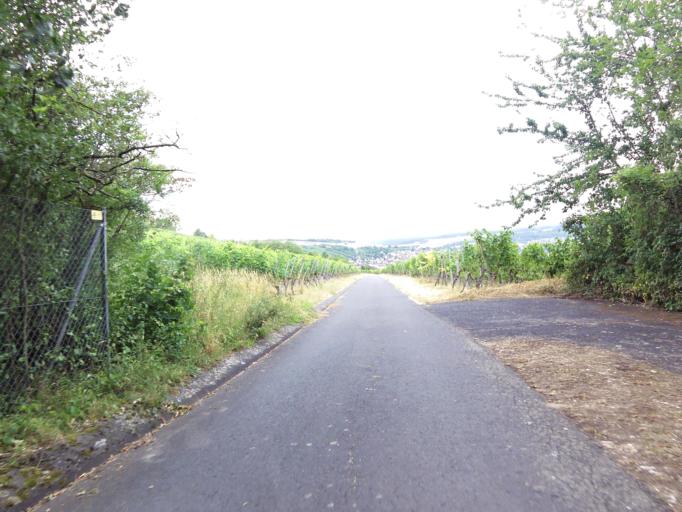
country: DE
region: Bavaria
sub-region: Regierungsbezirk Unterfranken
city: Randersacker
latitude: 49.7671
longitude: 9.9740
